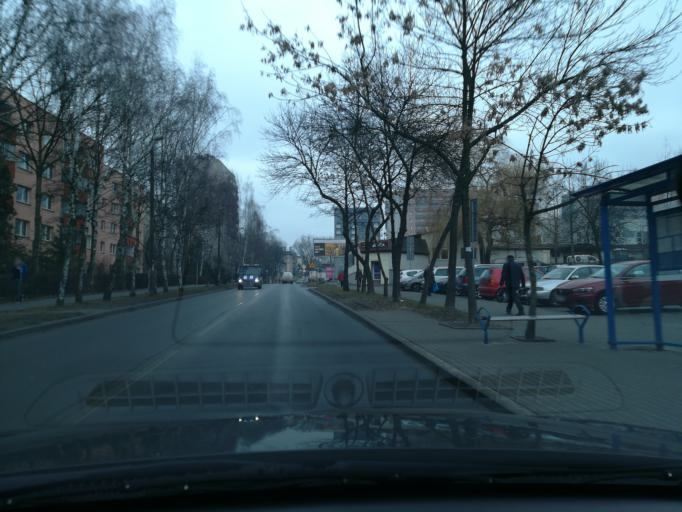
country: PL
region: Lesser Poland Voivodeship
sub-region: Krakow
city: Krakow
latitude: 50.0147
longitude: 19.9502
